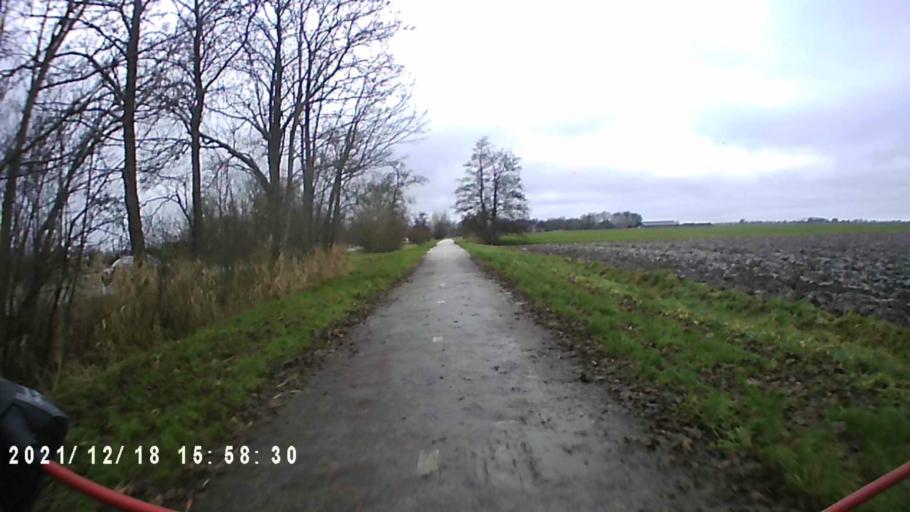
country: NL
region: Friesland
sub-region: Gemeente Dongeradeel
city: Anjum
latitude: 53.3371
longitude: 6.0925
